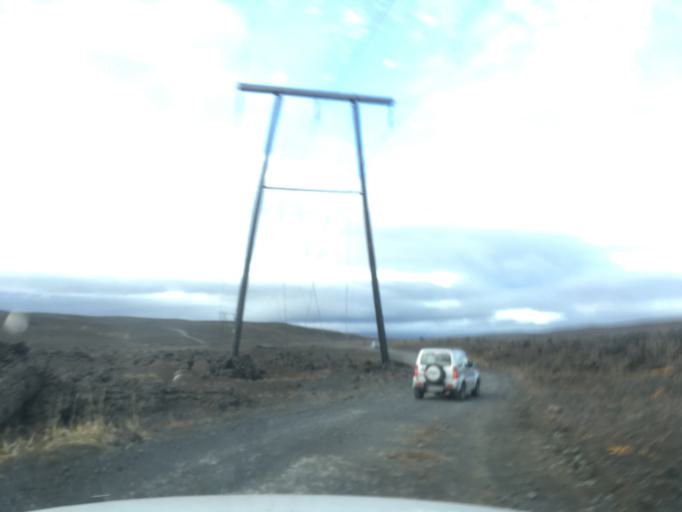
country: IS
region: South
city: Vestmannaeyjar
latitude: 64.1513
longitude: -19.1356
